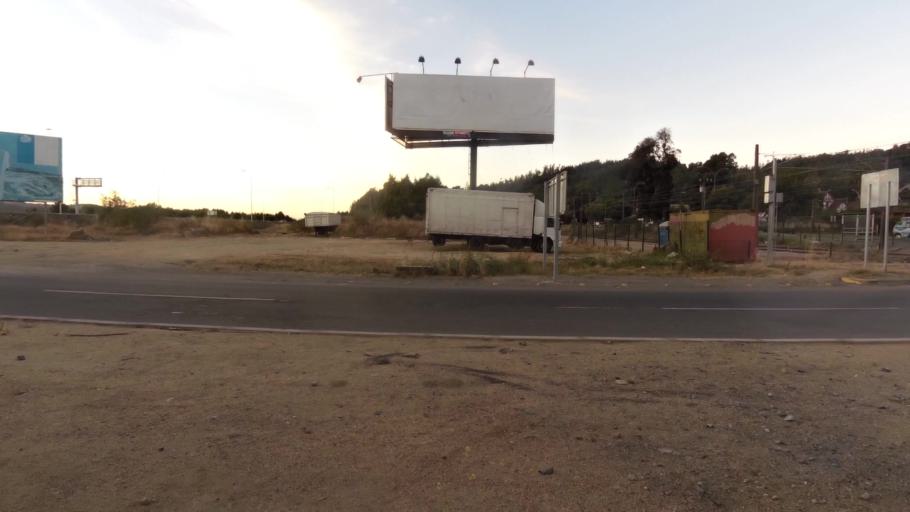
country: CL
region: Biobio
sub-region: Provincia de Concepcion
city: Concepcion
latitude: -36.8681
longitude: -73.0431
